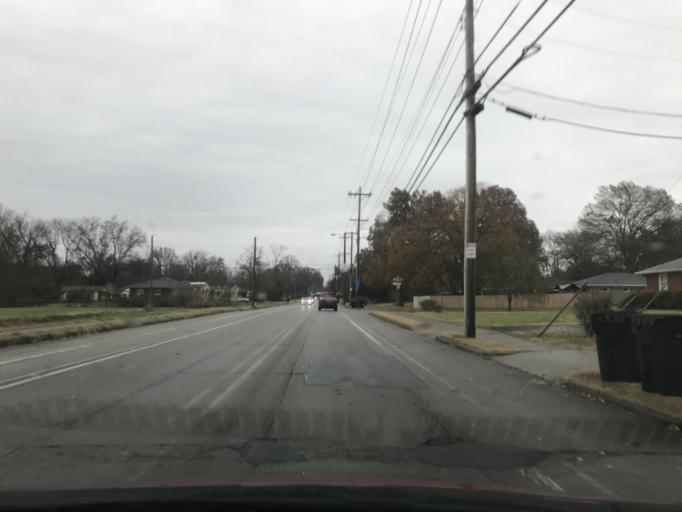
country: US
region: Kentucky
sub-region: Jefferson County
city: West Buechel
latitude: 38.2104
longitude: -85.6654
